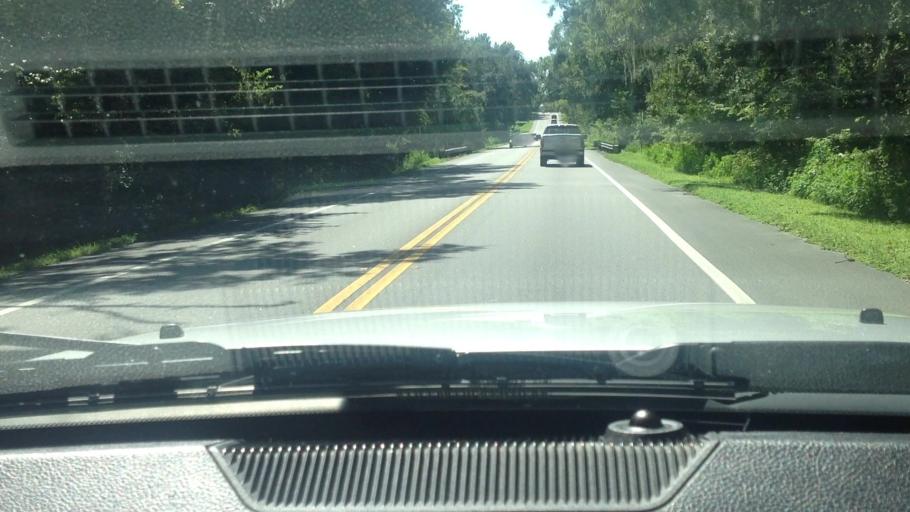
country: US
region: Florida
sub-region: Hillsborough County
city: Fish Hawk
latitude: 27.8699
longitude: -82.2108
